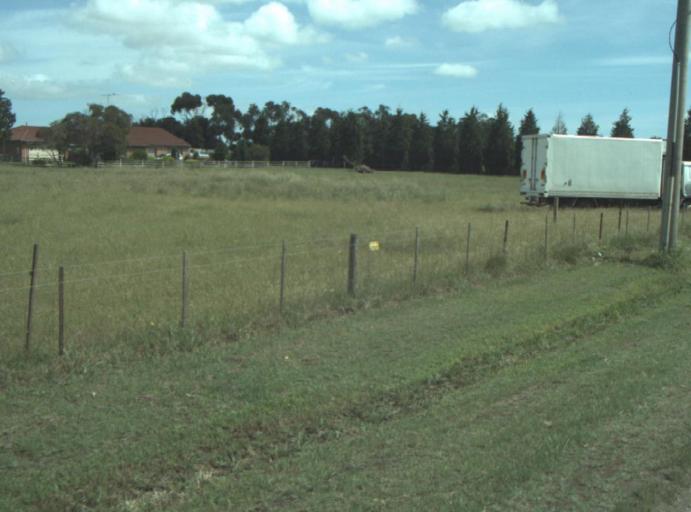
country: AU
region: Victoria
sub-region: Greater Geelong
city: Lara
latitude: -38.0378
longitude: 144.4308
